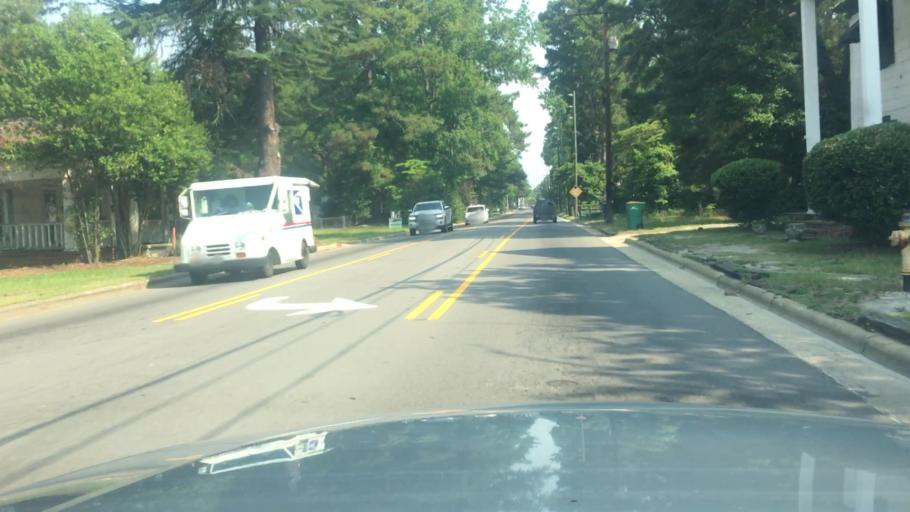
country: US
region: North Carolina
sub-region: Cumberland County
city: Hope Mills
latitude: 34.9665
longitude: -78.9442
